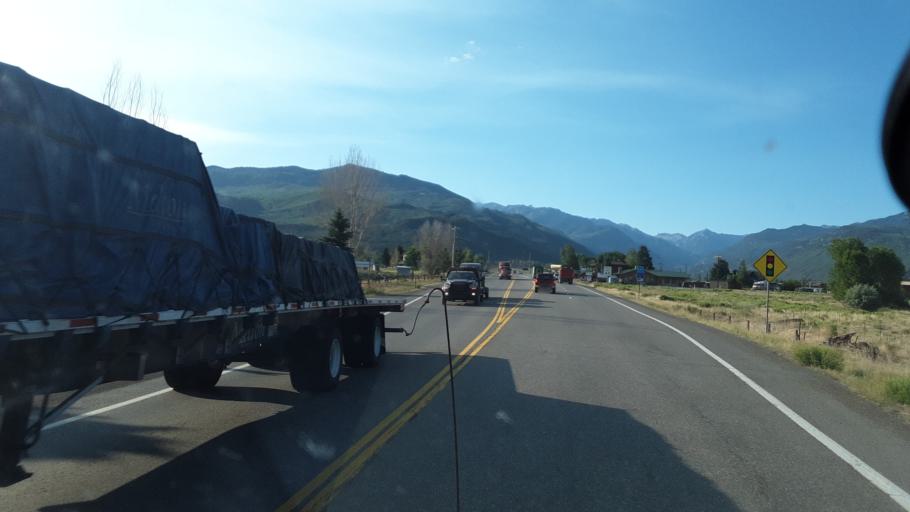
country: US
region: Colorado
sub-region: Ouray County
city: Ouray
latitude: 38.1546
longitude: -107.7514
